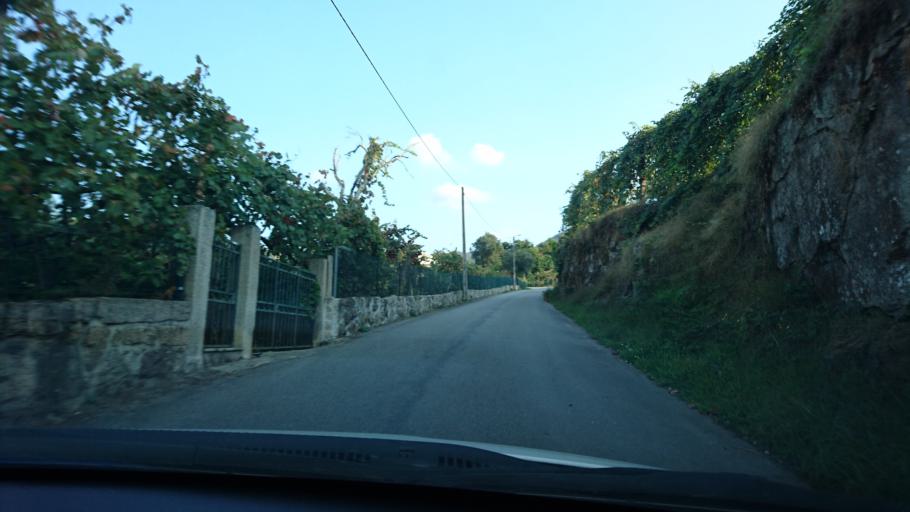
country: PT
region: Vila Real
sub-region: Mondim de Basto
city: Mondim de Basto
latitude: 41.4453
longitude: -7.9297
